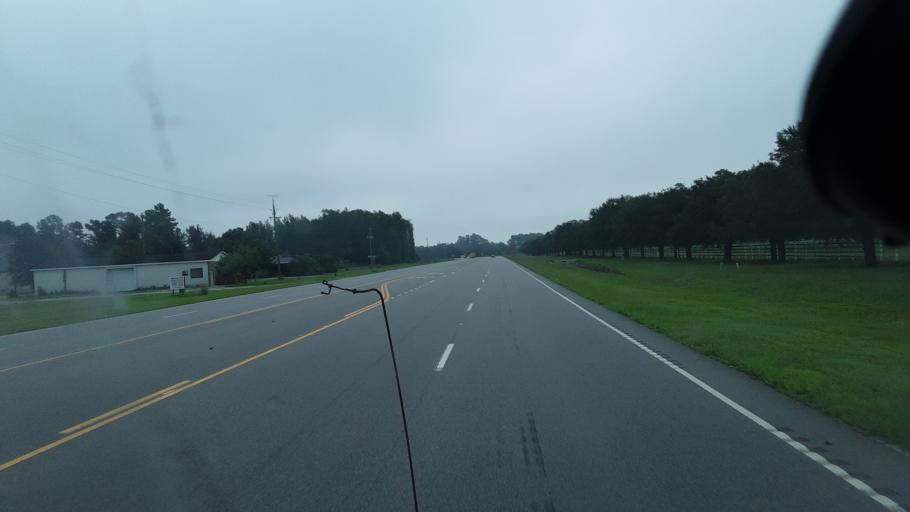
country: US
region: South Carolina
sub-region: Florence County
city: Johnsonville
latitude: 33.8820
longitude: -79.4622
